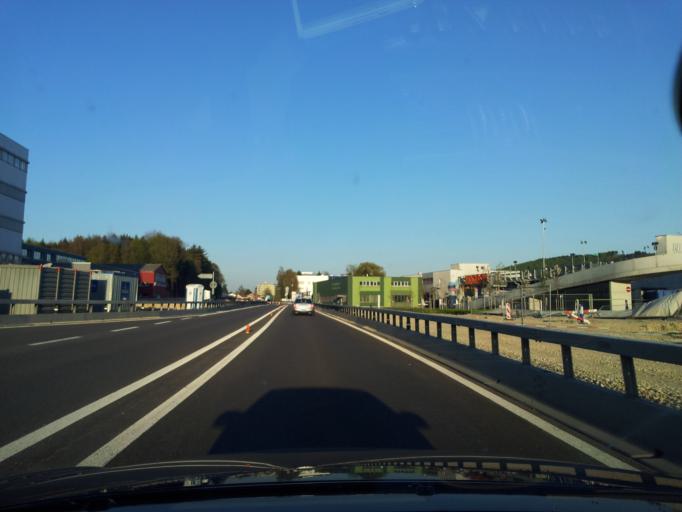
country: CH
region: Bern
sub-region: Biel/Bienne District
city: Brugg
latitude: 47.1215
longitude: 7.2663
